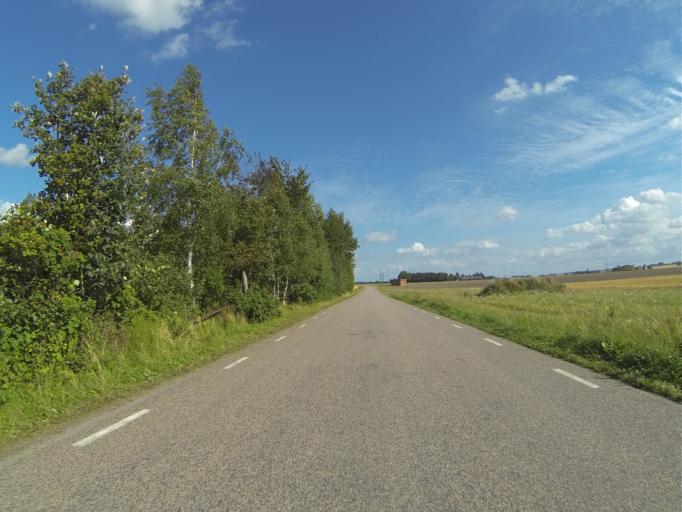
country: SE
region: Skane
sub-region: Lunds Kommun
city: Lund
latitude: 55.7775
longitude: 13.2129
